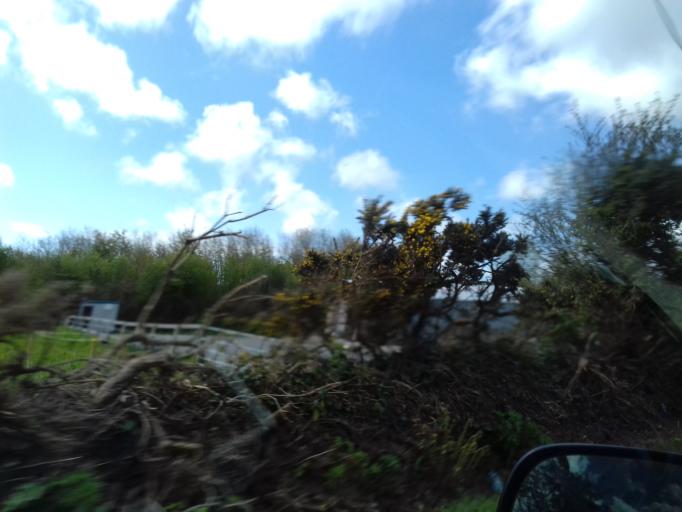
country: IE
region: Leinster
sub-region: Loch Garman
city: Loch Garman
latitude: 52.2824
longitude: -6.6730
